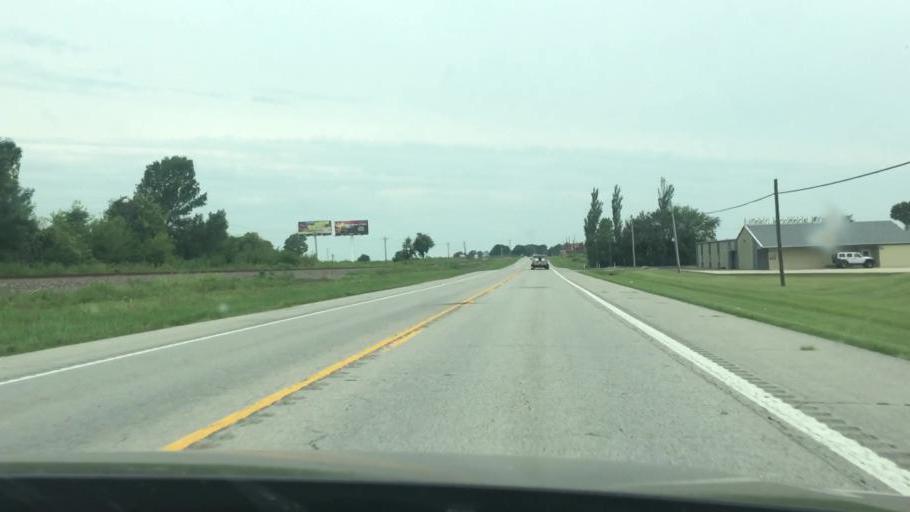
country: US
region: Missouri
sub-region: Pettis County
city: Sedalia
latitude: 38.6959
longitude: -93.1663
